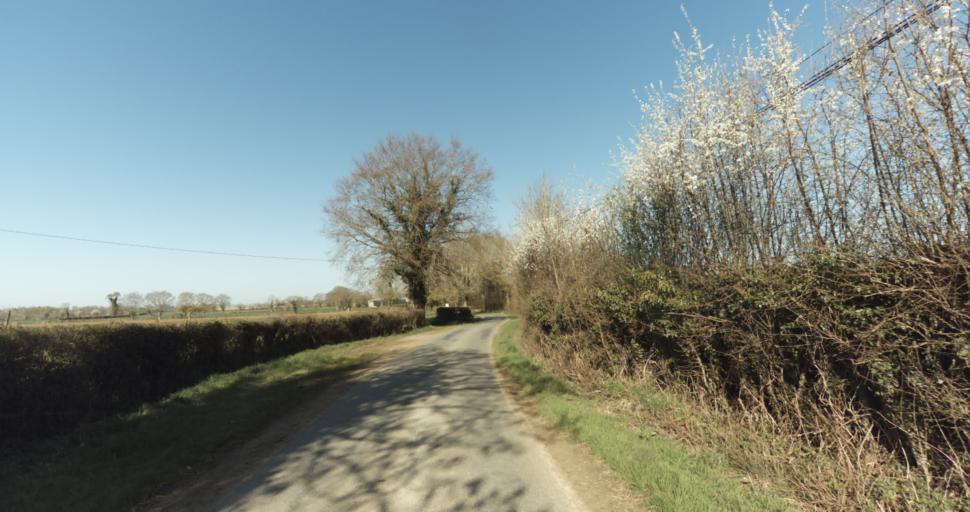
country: FR
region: Lower Normandy
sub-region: Departement du Calvados
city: Saint-Pierre-sur-Dives
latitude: 48.9661
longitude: 0.0257
